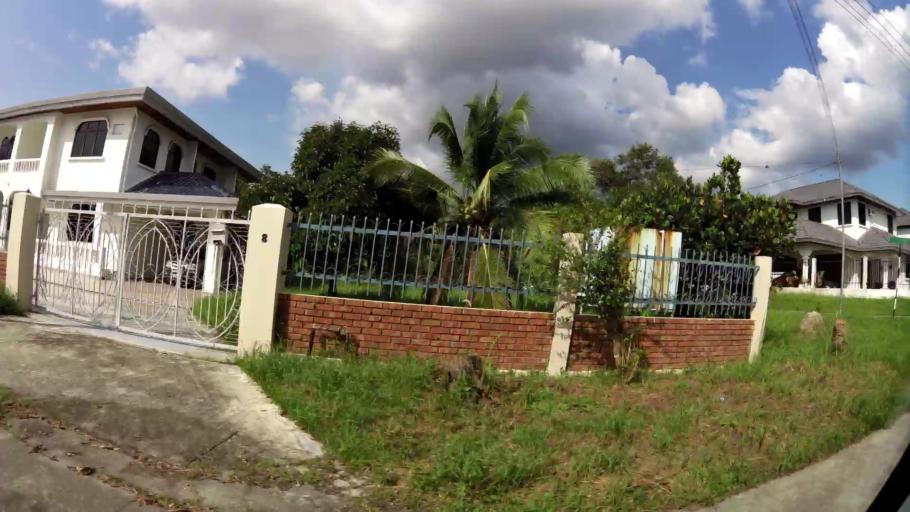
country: BN
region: Brunei and Muara
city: Bandar Seri Begawan
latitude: 4.9537
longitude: 114.9698
